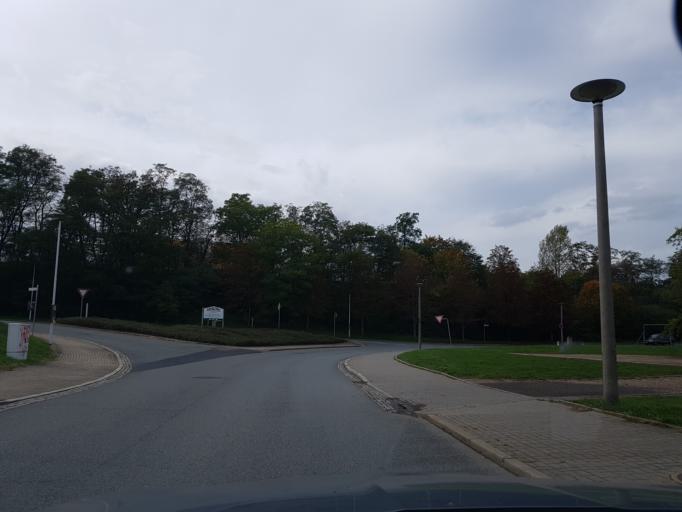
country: DE
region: Saxony
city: Riesa
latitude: 51.2972
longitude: 13.2930
